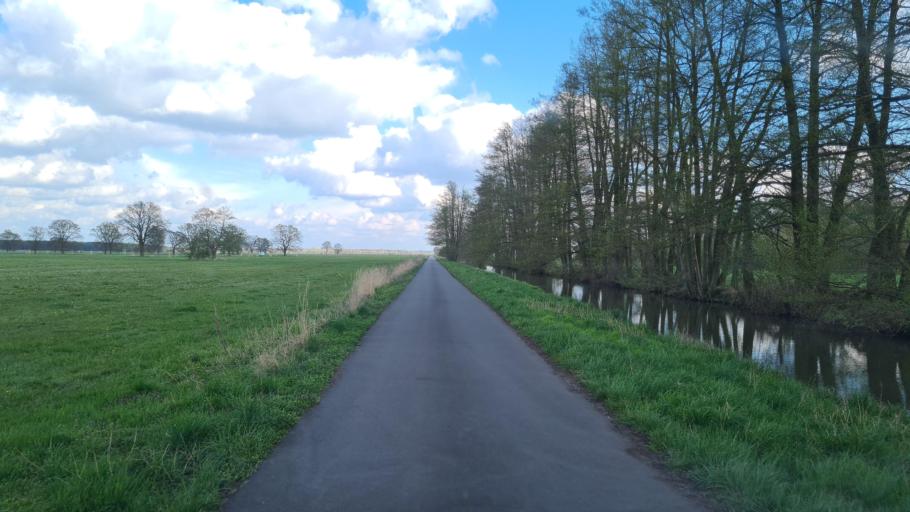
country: DE
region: Brandenburg
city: Herzberg
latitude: 51.7324
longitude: 13.2369
